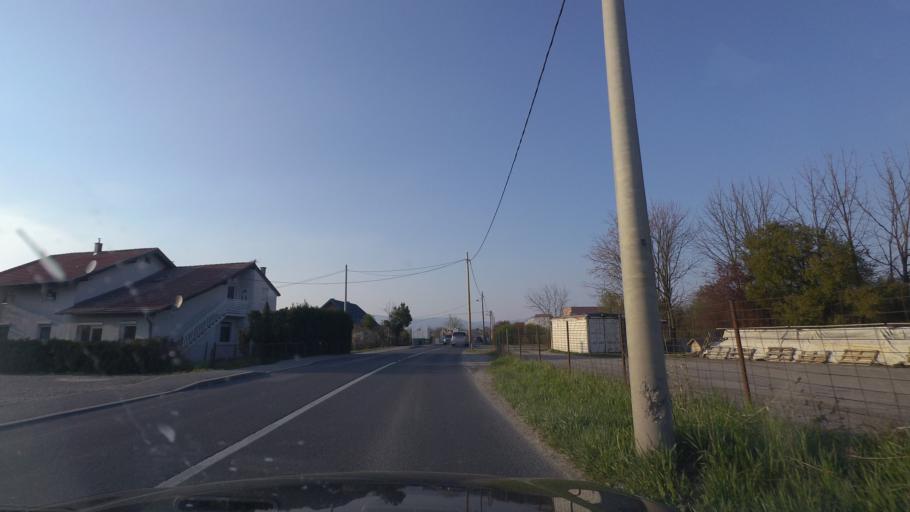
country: HR
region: Grad Zagreb
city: Dubrava
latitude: 45.8126
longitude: 16.0665
